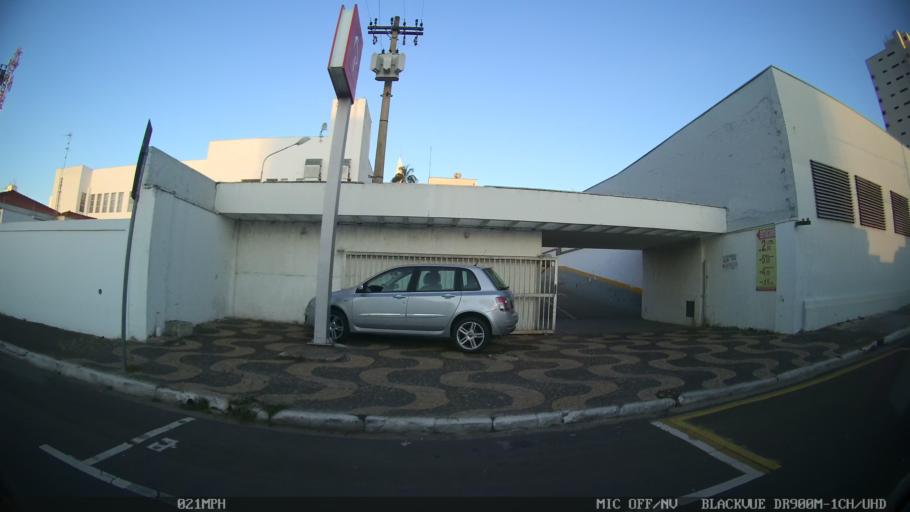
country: BR
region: Sao Paulo
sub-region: Santa Barbara D'Oeste
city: Santa Barbara d'Oeste
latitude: -22.7539
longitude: -47.4149
